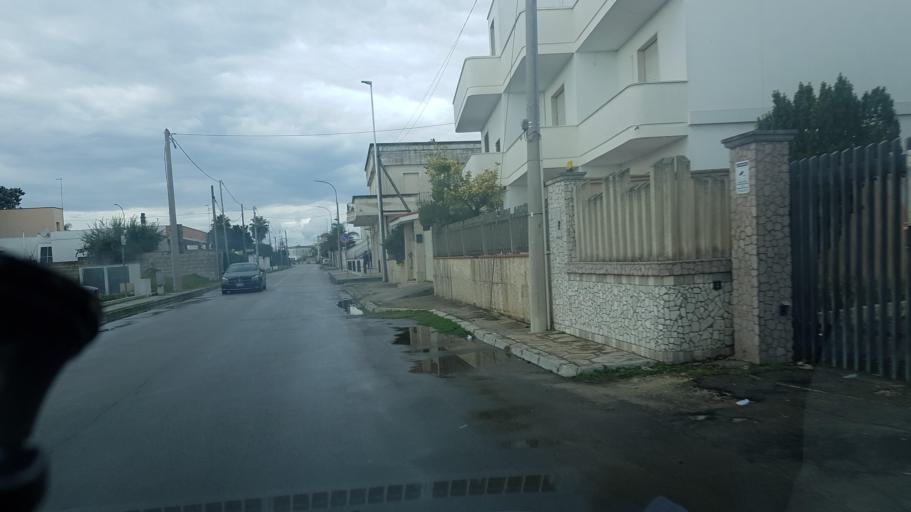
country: IT
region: Apulia
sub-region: Provincia di Lecce
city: Salice Salentino
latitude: 40.3913
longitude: 17.9586
